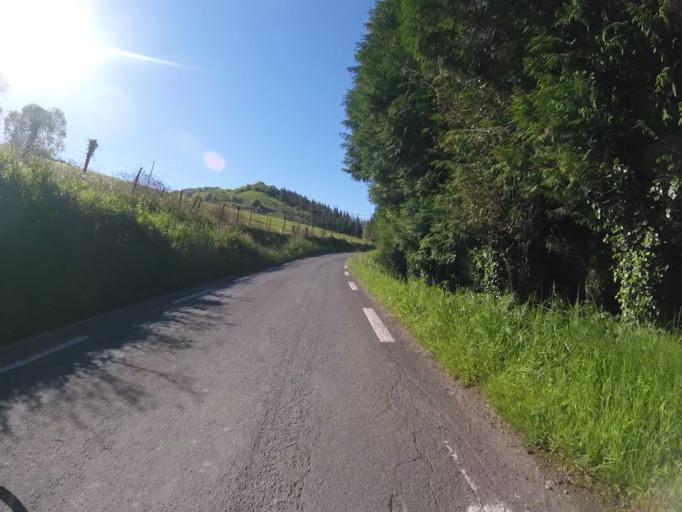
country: ES
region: Basque Country
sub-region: Provincia de Guipuzcoa
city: Aizarnazabal
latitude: 43.2281
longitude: -2.2143
